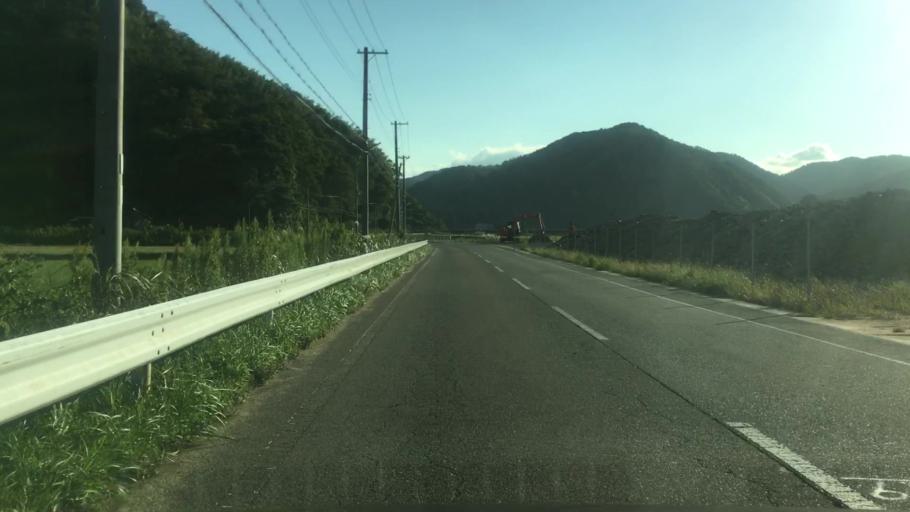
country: JP
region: Hyogo
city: Toyooka
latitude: 35.6112
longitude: 134.8095
